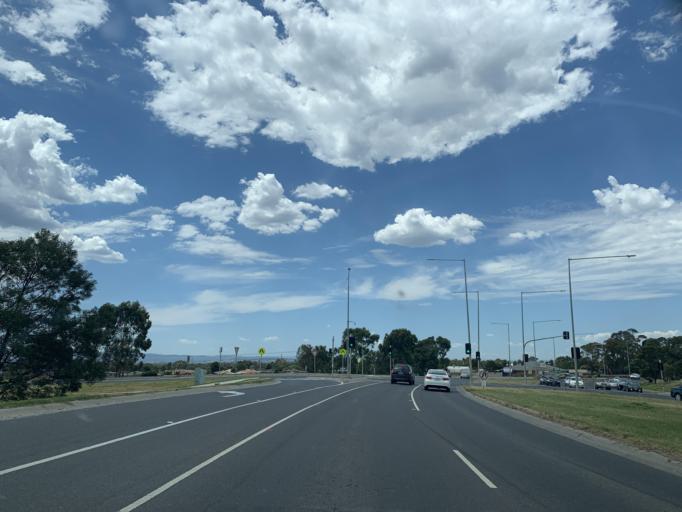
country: AU
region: Victoria
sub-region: Casey
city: Cranbourne West
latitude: -38.1104
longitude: 145.2527
